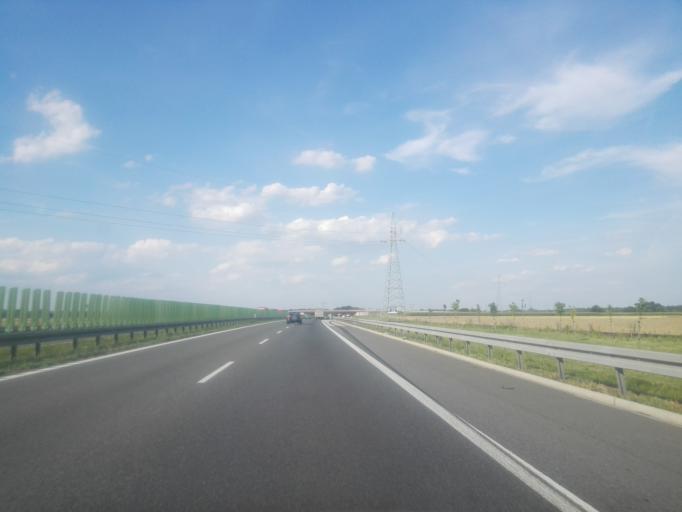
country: PL
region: Lower Silesian Voivodeship
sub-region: Powiat wroclawski
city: Mirkow
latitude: 51.2115
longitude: 17.1307
